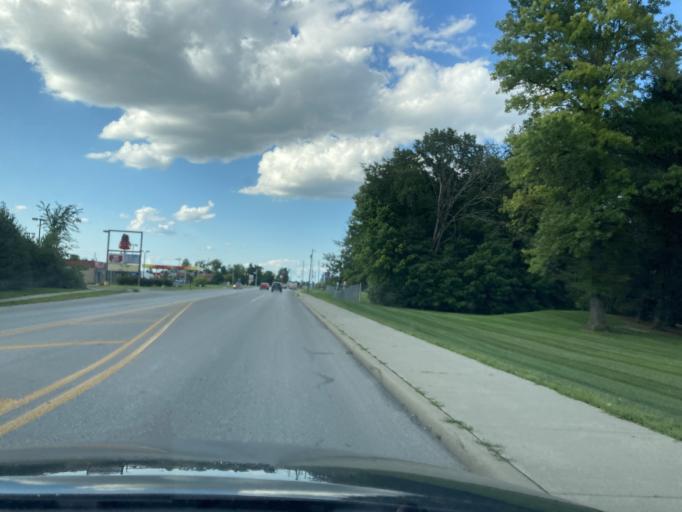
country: US
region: Indiana
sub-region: Boone County
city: Zionsville
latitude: 39.8796
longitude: -86.2443
